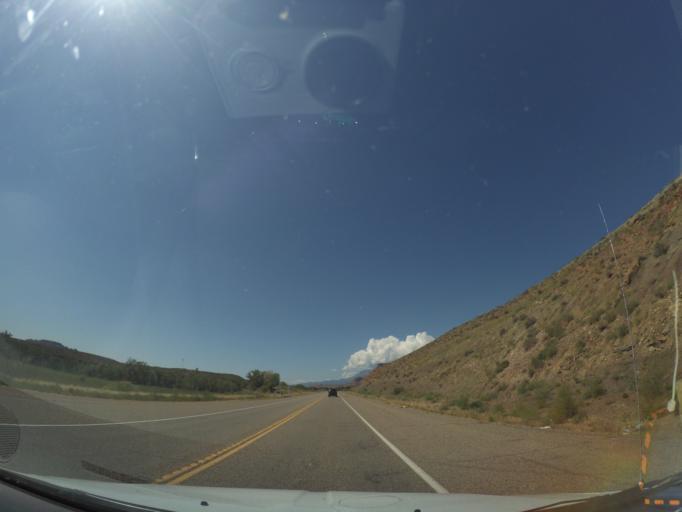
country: US
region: Utah
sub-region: Washington County
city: LaVerkin
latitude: 37.1970
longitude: -113.1618
